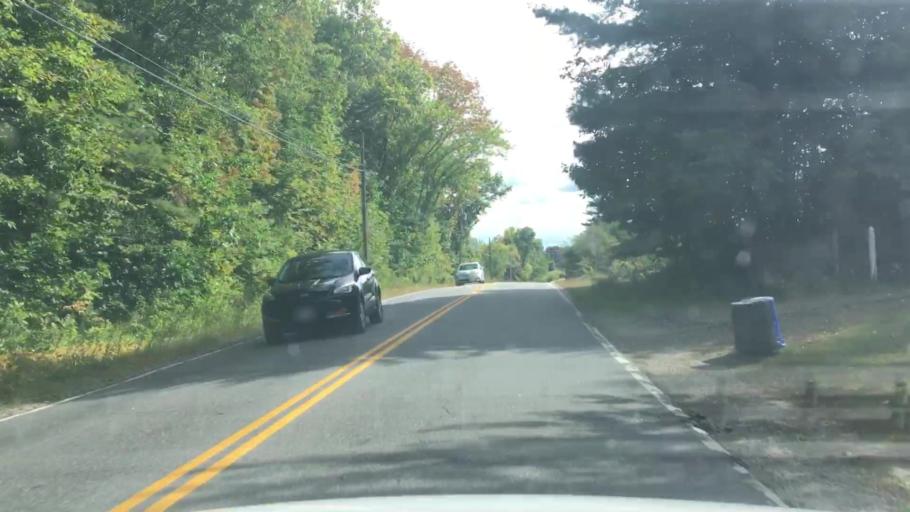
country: US
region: Maine
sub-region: Androscoggin County
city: Lisbon
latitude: 44.0271
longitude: -70.1822
